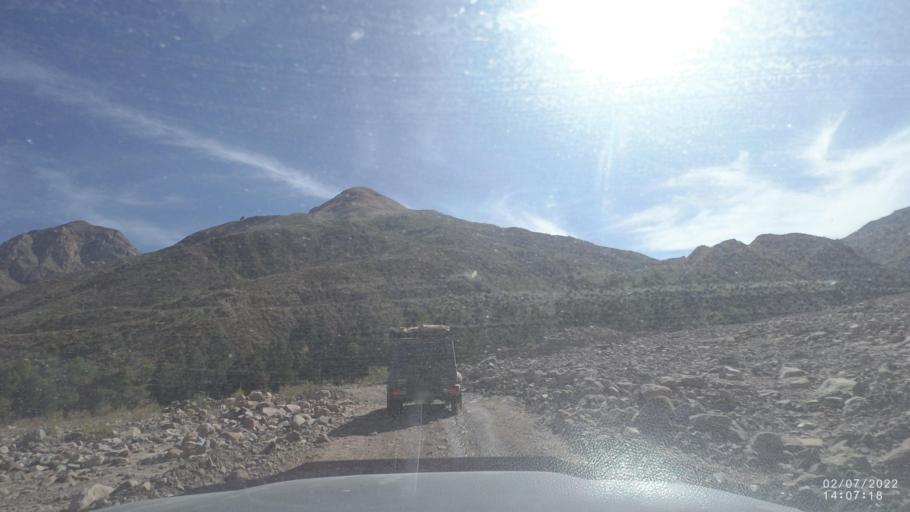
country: BO
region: Cochabamba
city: Irpa Irpa
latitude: -17.8188
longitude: -66.4004
